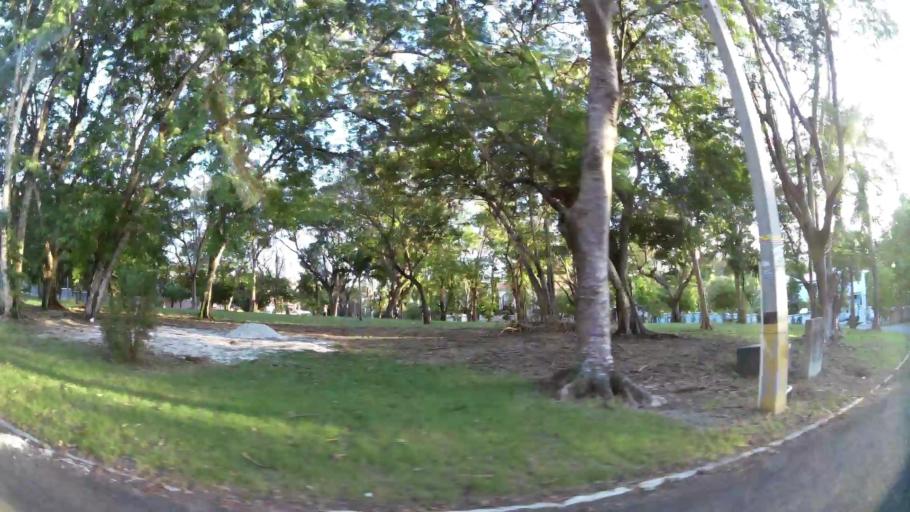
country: DO
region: Nacional
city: La Agustina
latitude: 18.4905
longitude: -69.9608
